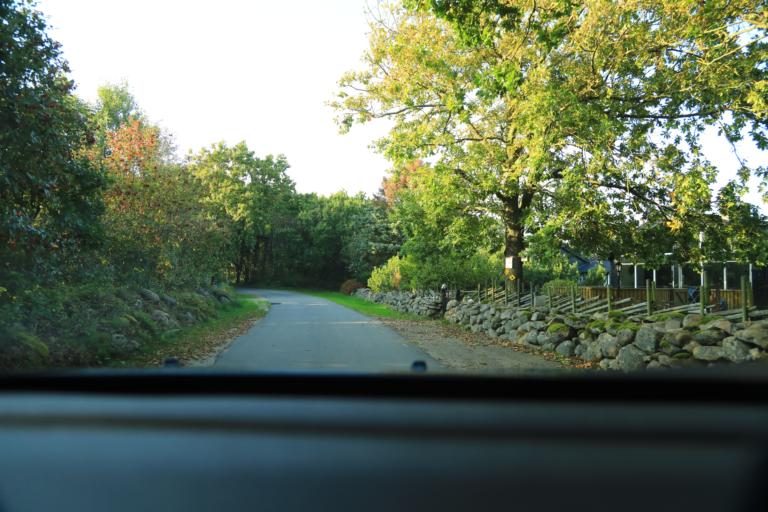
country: SE
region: Halland
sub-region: Varbergs Kommun
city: Traslovslage
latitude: 57.0395
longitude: 12.2968
